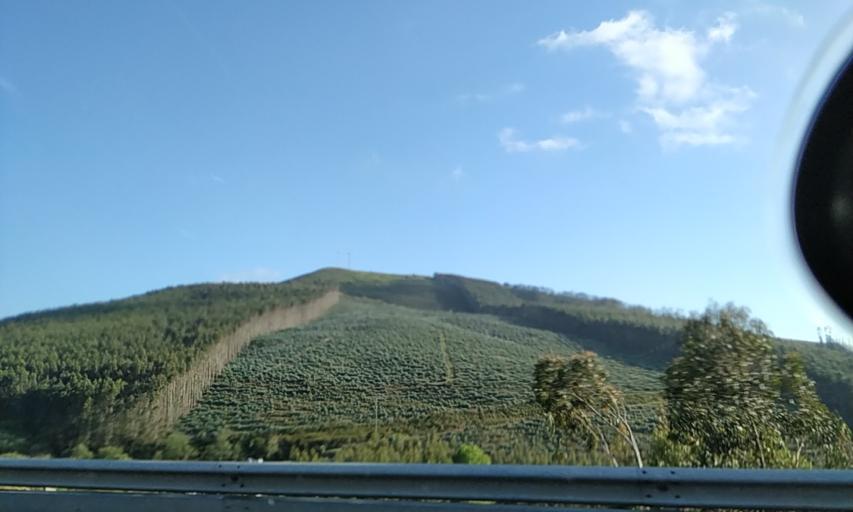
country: PT
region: Lisbon
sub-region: Torres Vedras
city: Torres Vedras
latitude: 39.0303
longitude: -9.2234
